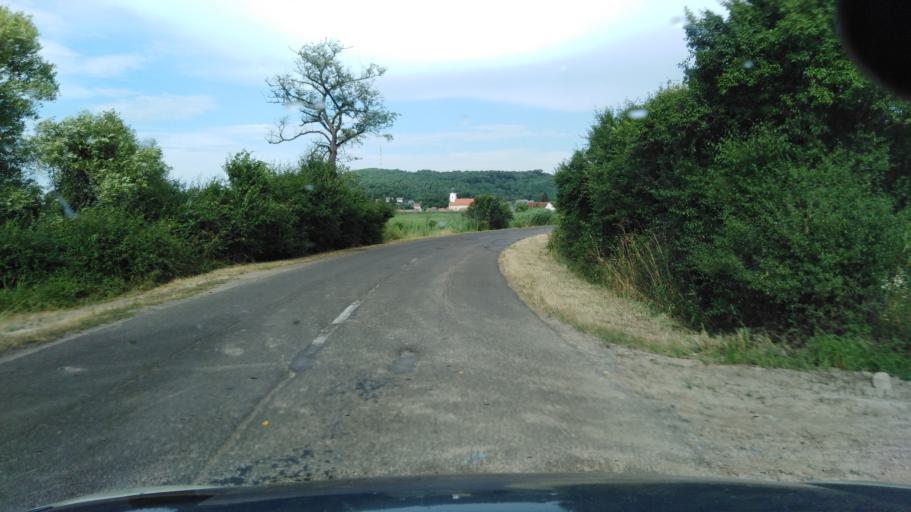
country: HU
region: Nograd
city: Karancskeszi
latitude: 48.2085
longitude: 19.5863
